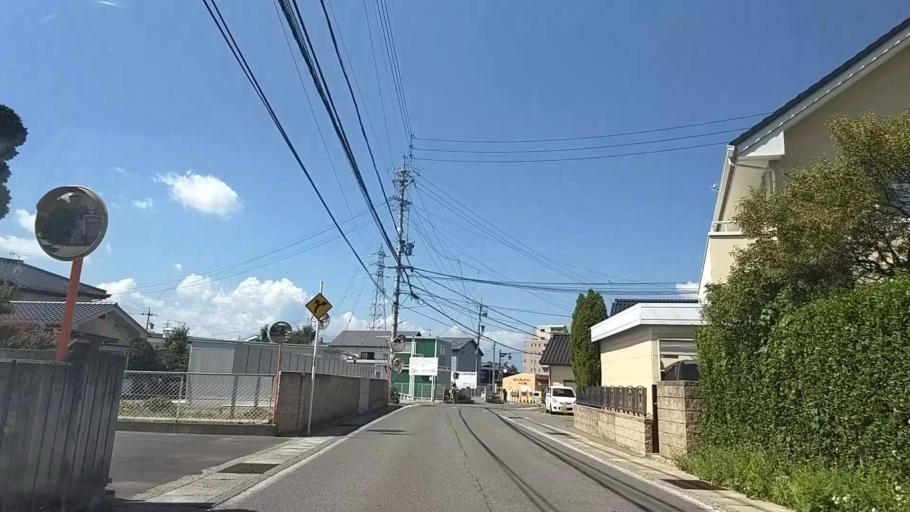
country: JP
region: Nagano
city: Matsumoto
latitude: 36.2373
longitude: 137.9893
